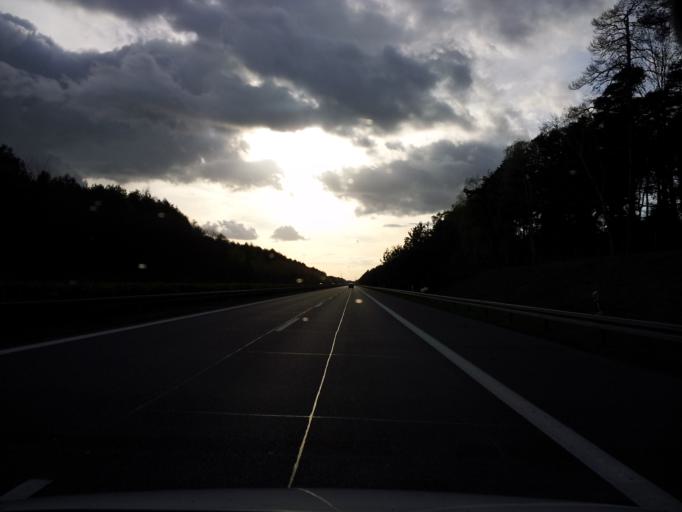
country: DE
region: Brandenburg
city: Kolkwitz
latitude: 51.7260
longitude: 14.2260
